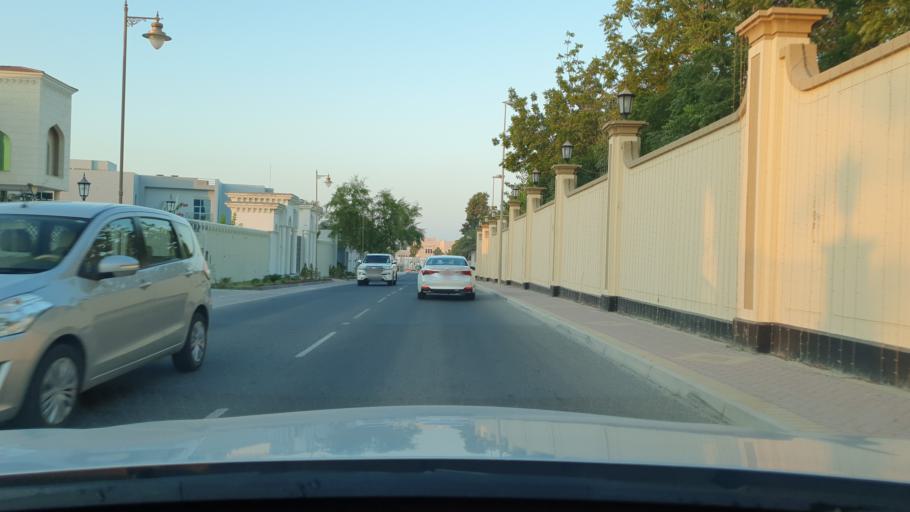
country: BH
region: Northern
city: Ar Rifa'
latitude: 26.1384
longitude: 50.5326
